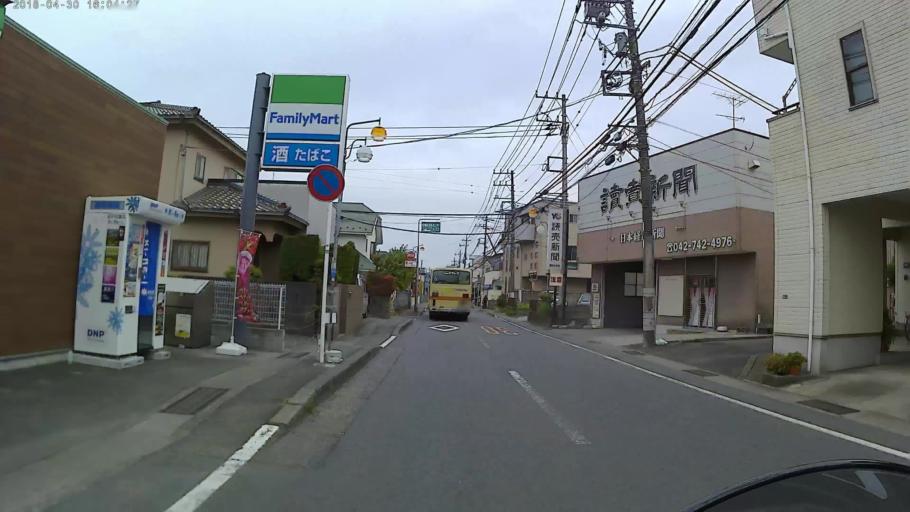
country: JP
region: Kanagawa
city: Minami-rinkan
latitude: 35.5095
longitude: 139.4241
